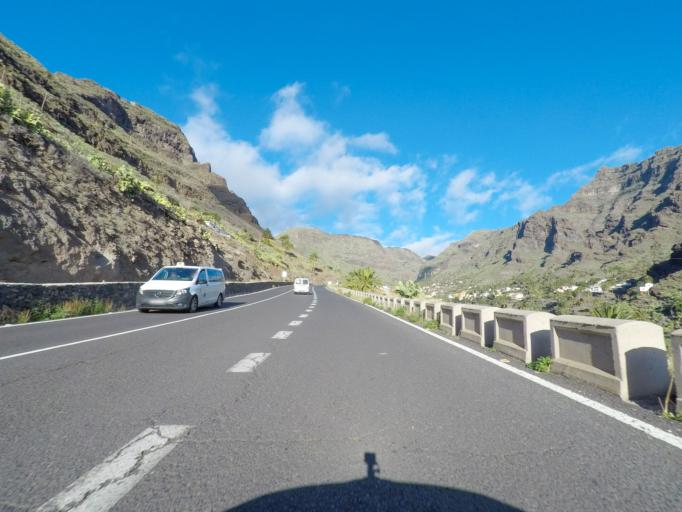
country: ES
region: Canary Islands
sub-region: Provincia de Santa Cruz de Tenerife
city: Vallehermosa
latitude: 28.1090
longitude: -17.3228
